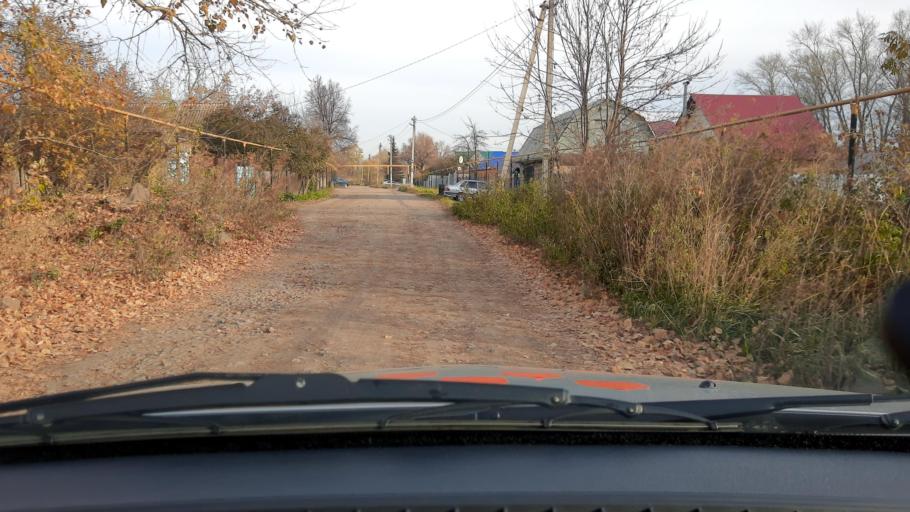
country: RU
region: Bashkortostan
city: Ufa
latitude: 54.8278
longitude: 56.1318
